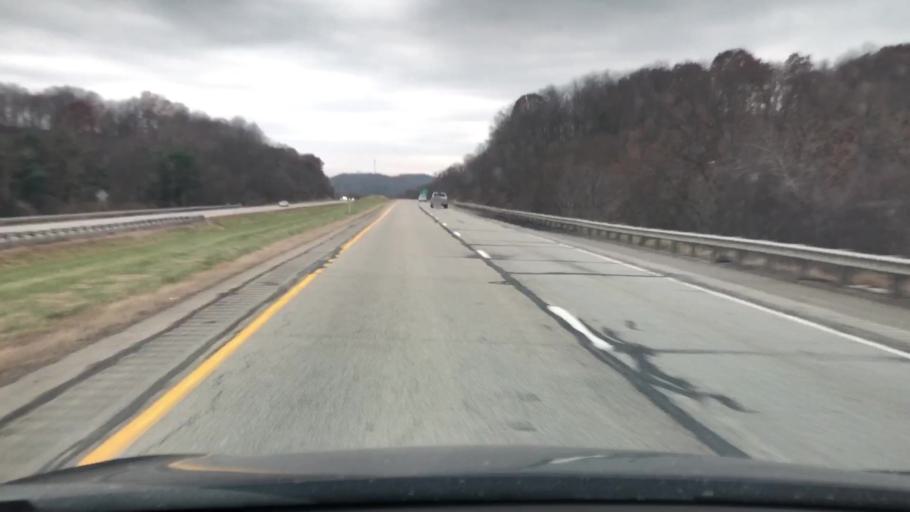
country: US
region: Pennsylvania
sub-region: Armstrong County
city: Ford City
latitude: 40.7772
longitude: -79.5978
